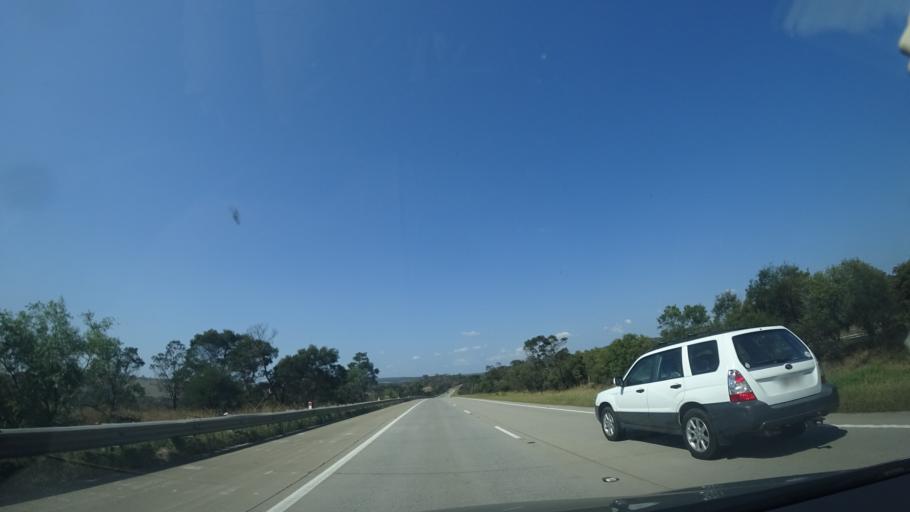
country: AU
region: New South Wales
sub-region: Wingecarribee
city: Bowral
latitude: -34.4529
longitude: 150.3672
